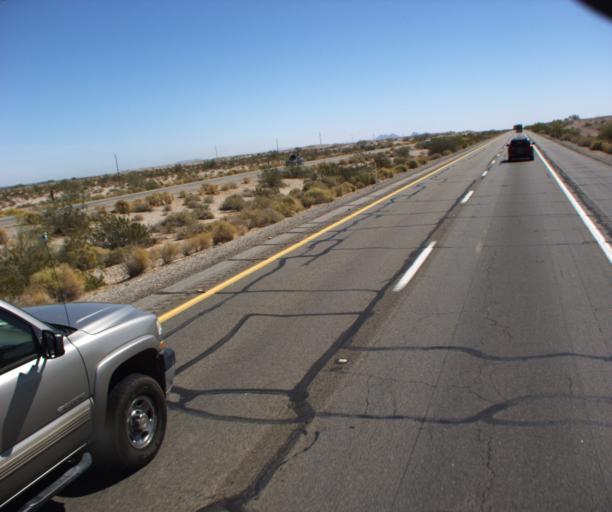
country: US
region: Arizona
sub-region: Yuma County
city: Wellton
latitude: 32.6578
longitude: -114.2466
